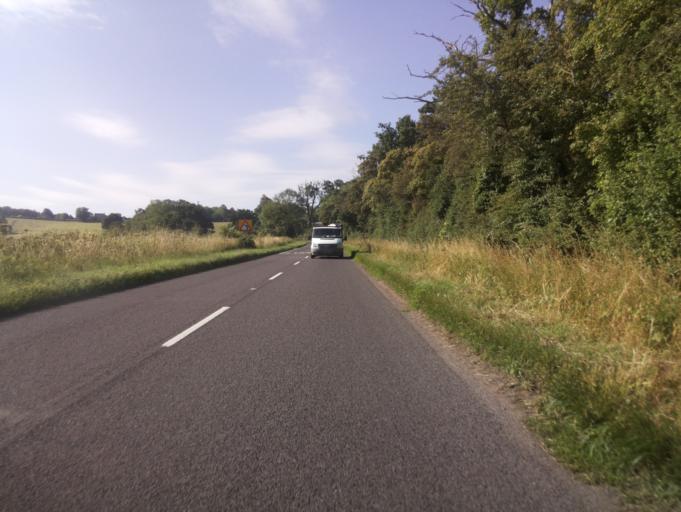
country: GB
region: England
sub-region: Oxfordshire
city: Faringdon
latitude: 51.6668
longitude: -1.5863
